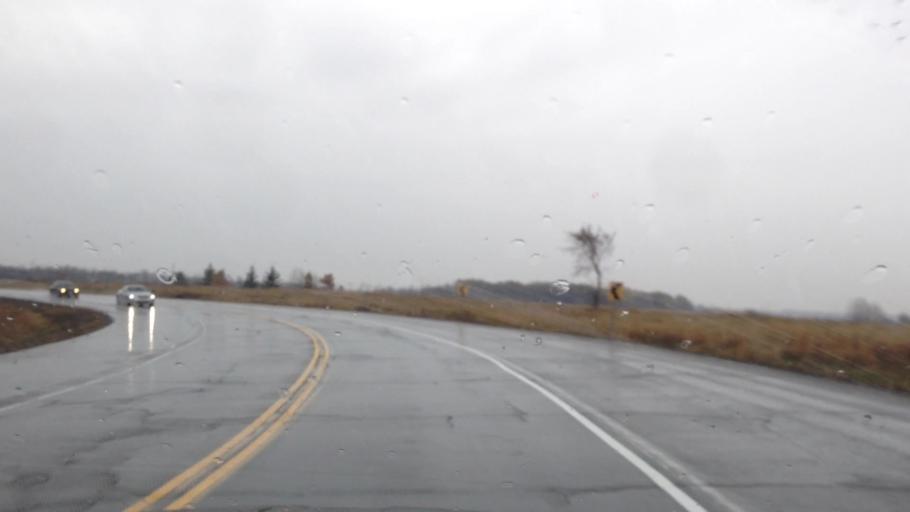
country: CA
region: Ontario
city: Clarence-Rockland
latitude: 45.4721
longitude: -75.4405
